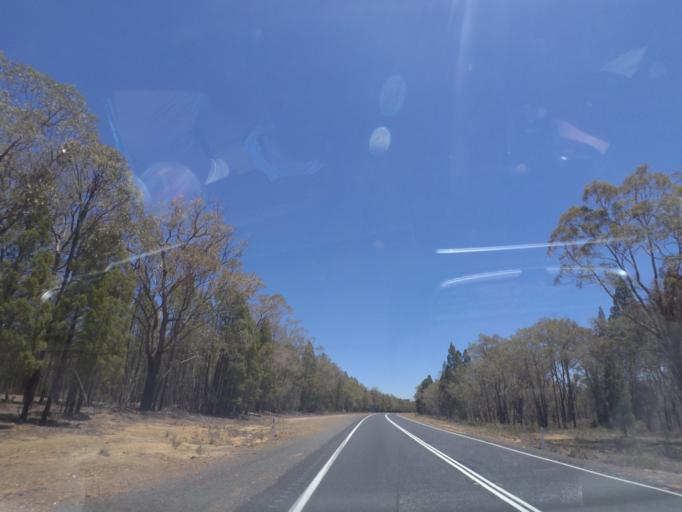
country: AU
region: New South Wales
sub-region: Warrumbungle Shire
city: Coonabarabran
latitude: -31.1979
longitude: 149.3483
